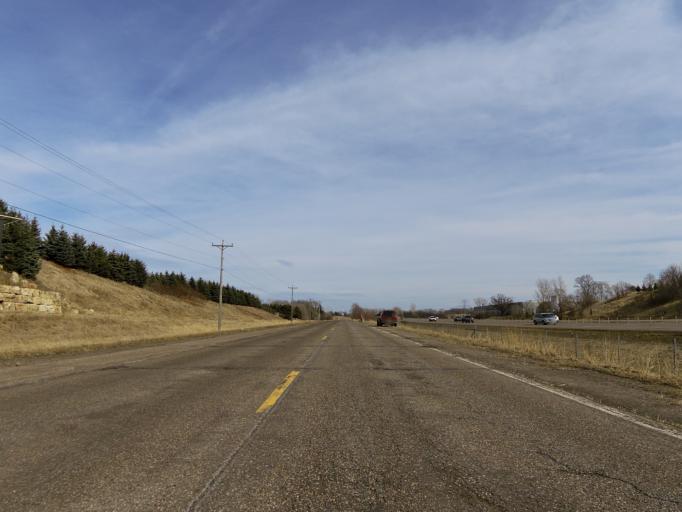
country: US
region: Minnesota
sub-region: Washington County
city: Lake Elmo
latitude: 44.9490
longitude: -92.8358
